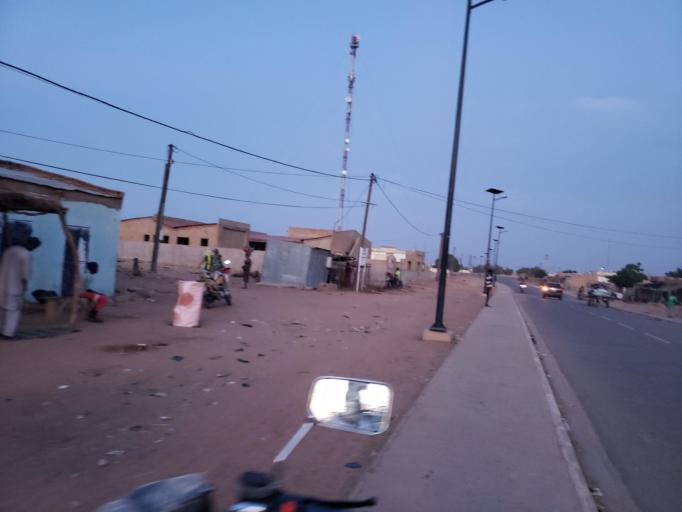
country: SN
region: Matam
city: Ranerou
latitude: 15.2985
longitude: -13.9591
